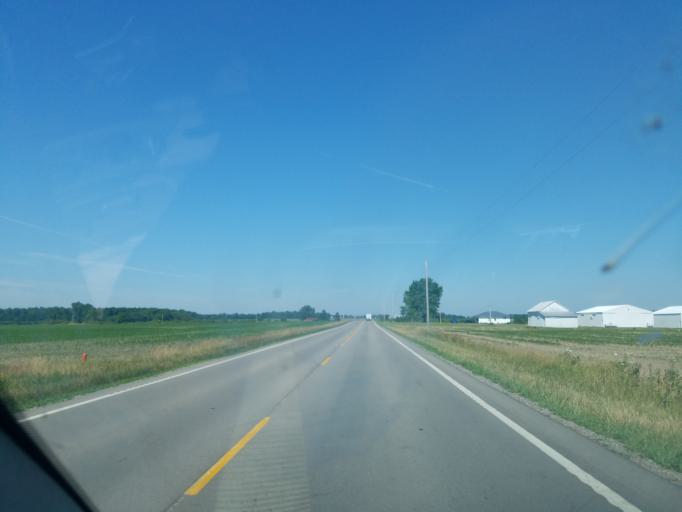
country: US
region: Ohio
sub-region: Shelby County
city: Jackson Center
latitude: 40.4393
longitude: -83.9887
